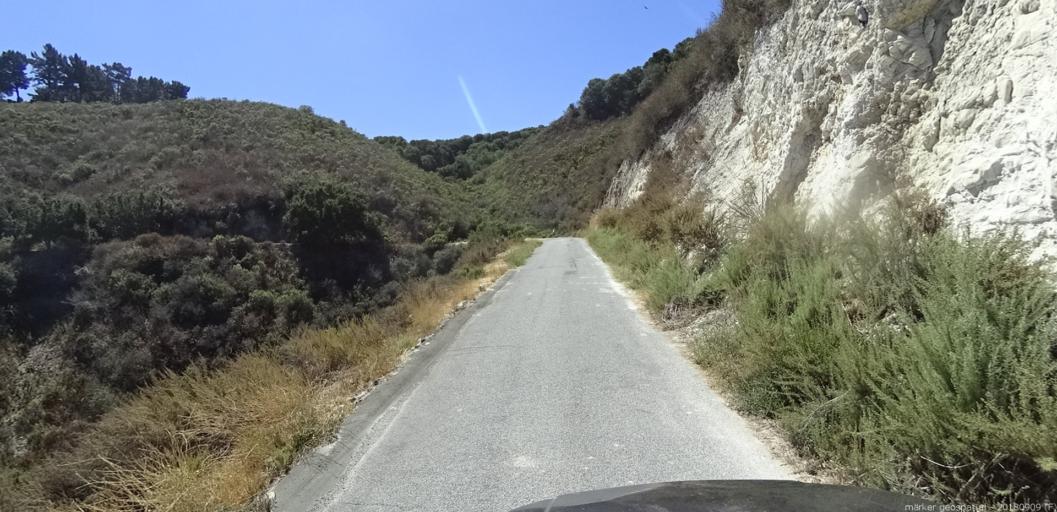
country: US
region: California
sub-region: Monterey County
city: Carmel Valley Village
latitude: 36.5536
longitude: -121.7486
